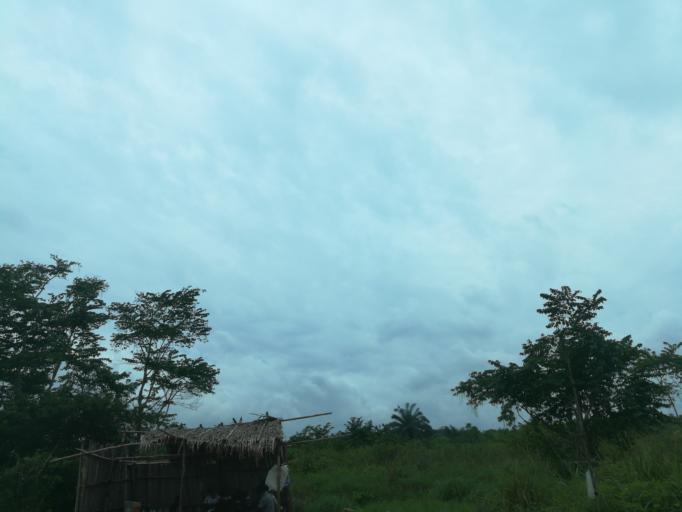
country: NG
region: Lagos
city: Ejirin
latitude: 6.6588
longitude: 3.8179
